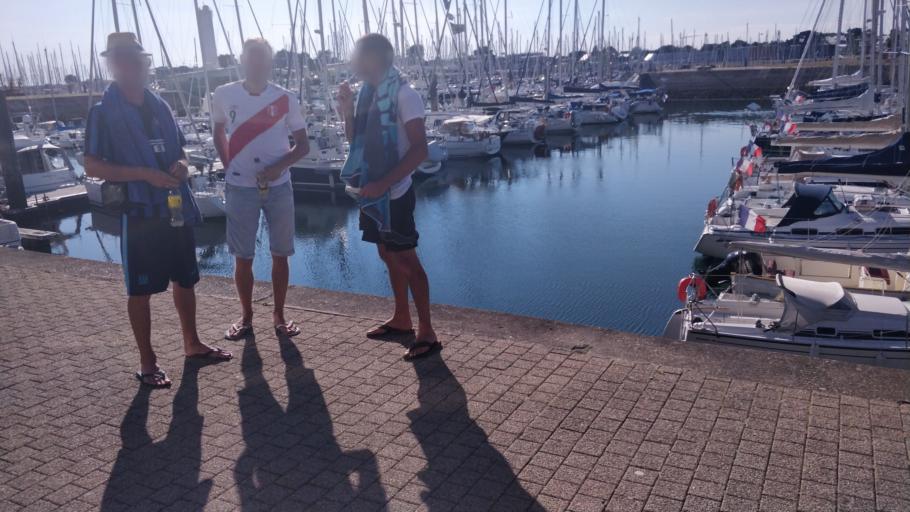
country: FR
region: Brittany
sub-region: Departement du Morbihan
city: Arzon
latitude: 47.5441
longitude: -2.8910
